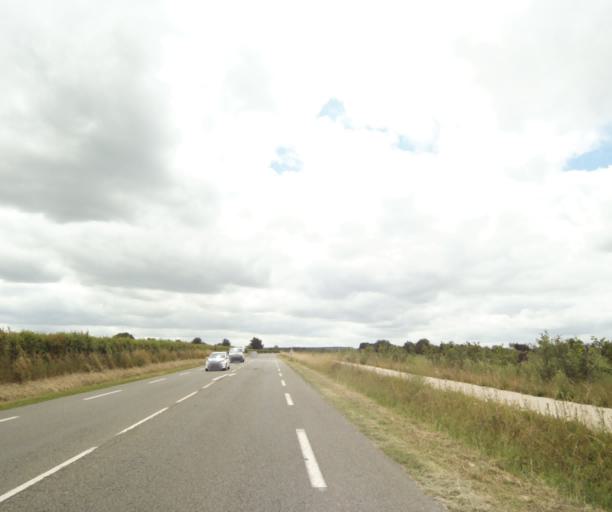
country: FR
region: Ile-de-France
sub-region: Departement des Yvelines
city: Bailly
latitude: 48.8280
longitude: 2.0845
